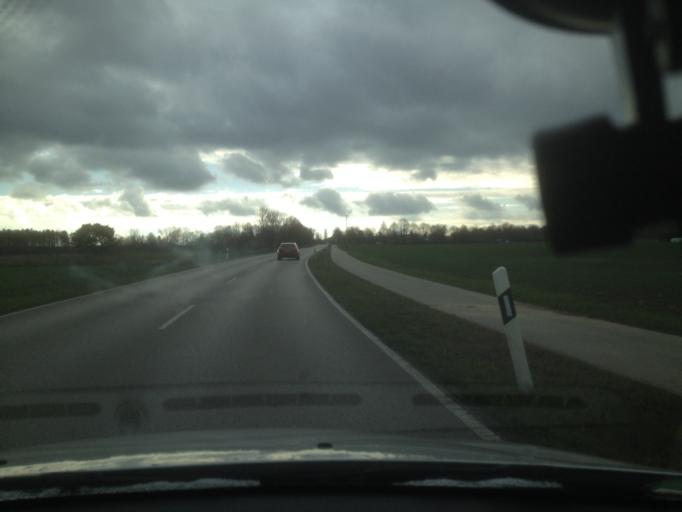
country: DE
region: Bavaria
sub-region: Swabia
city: Konigsbrunn
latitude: 48.2771
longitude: 10.9014
